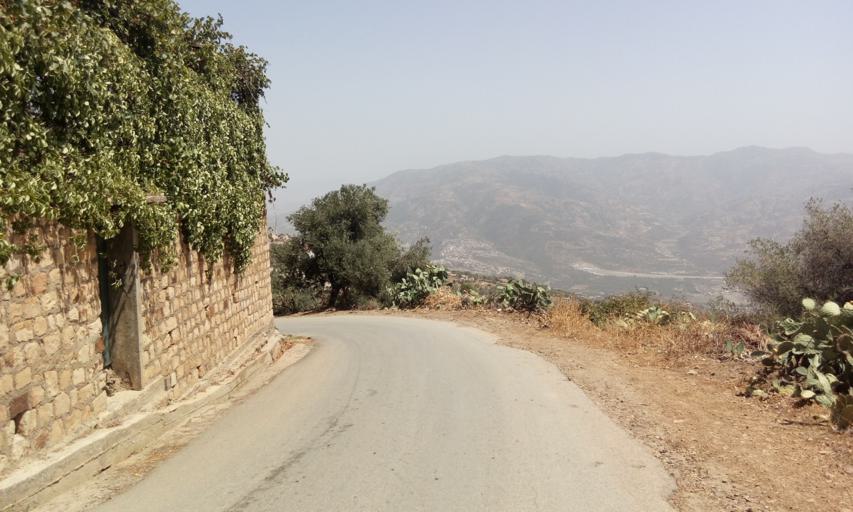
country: DZ
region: Tizi Ouzou
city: Chemini
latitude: 36.6058
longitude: 4.6349
